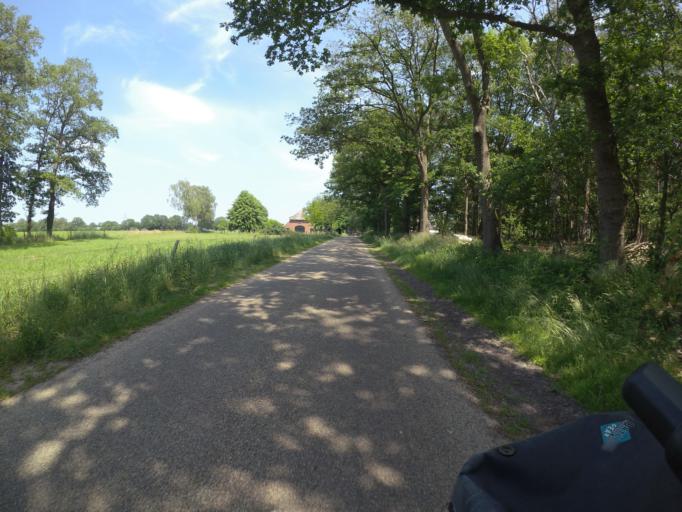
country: NL
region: Overijssel
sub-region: Gemeente Hof van Twente
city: Markelo
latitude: 52.2753
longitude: 6.4631
